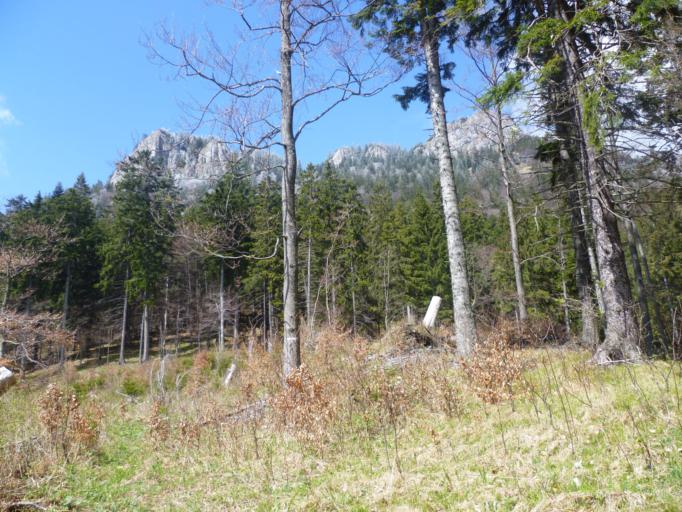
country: SK
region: Zilinsky
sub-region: Okres Dolny Kubin
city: Dolny Kubin
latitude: 49.1509
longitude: 19.3489
